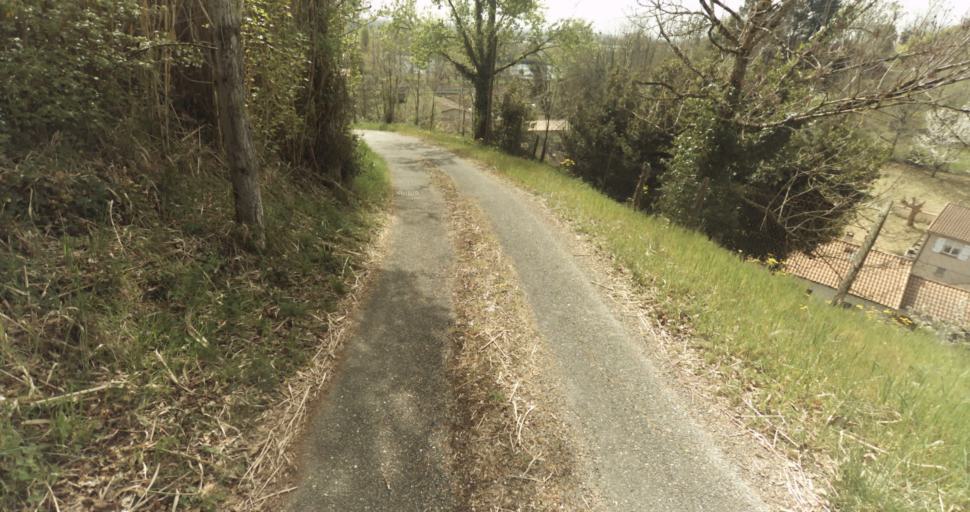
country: FR
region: Midi-Pyrenees
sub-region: Departement du Tarn-et-Garonne
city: Moissac
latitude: 44.1027
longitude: 1.0727
